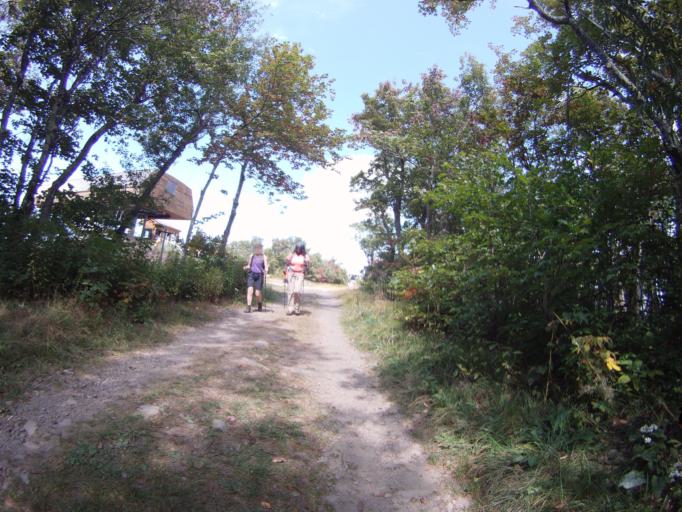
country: US
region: New York
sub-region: Ulster County
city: Woodstock
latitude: 42.1995
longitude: -74.2314
